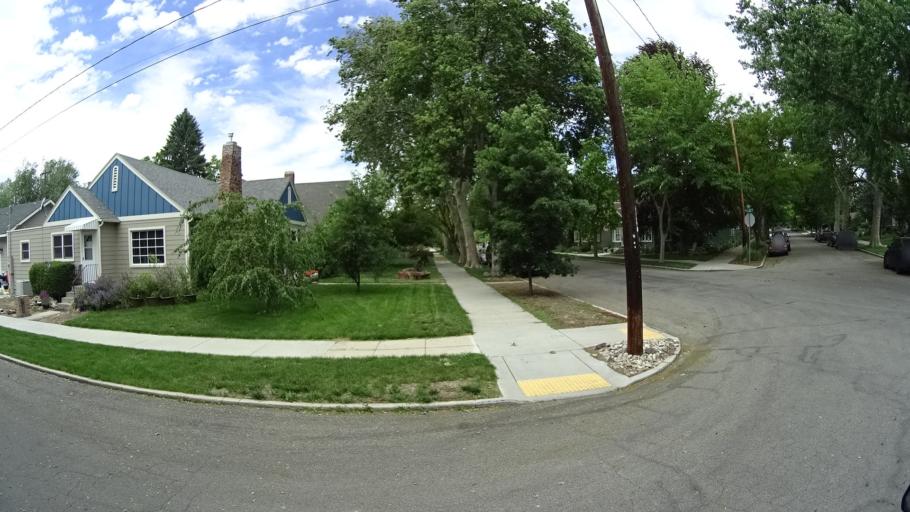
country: US
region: Idaho
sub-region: Ada County
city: Boise
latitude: 43.6281
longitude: -116.2158
